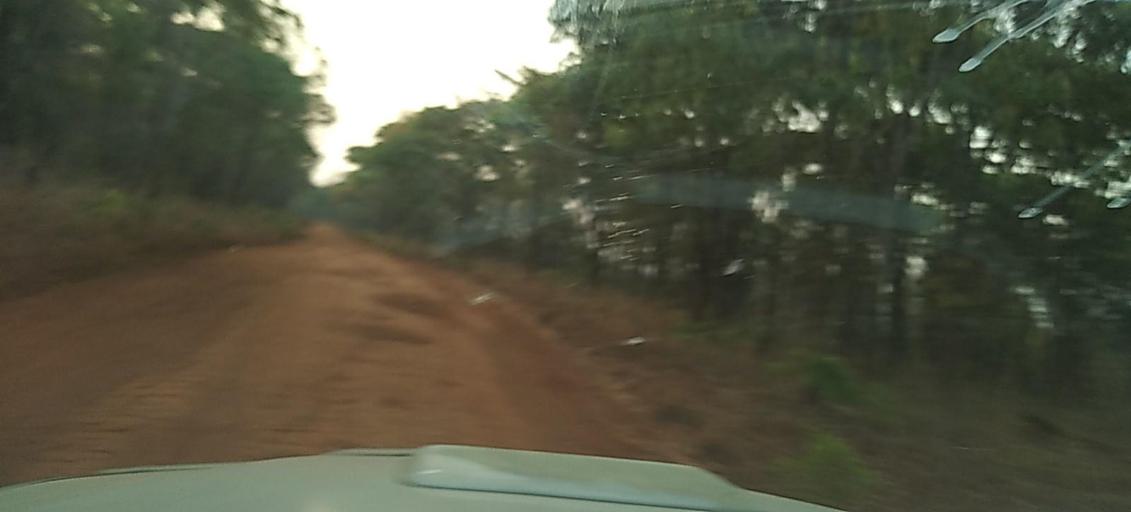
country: ZM
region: North-Western
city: Kasempa
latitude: -13.0786
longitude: 26.3919
